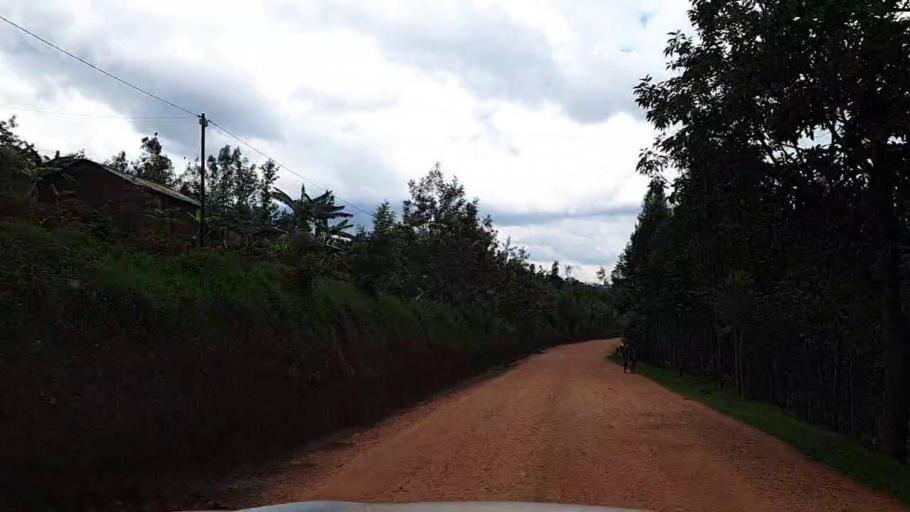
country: RW
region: Southern Province
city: Nyanza
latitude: -2.4131
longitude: 29.6719
